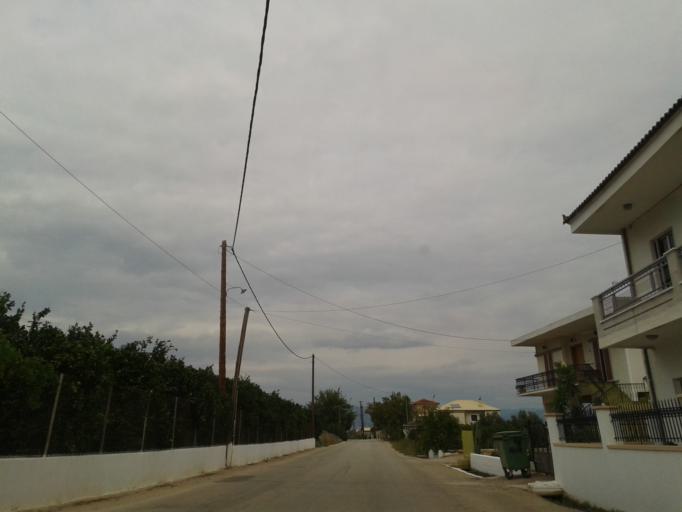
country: GR
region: Peloponnese
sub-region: Nomos Argolidos
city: Argos
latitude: 37.6030
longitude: 22.6953
